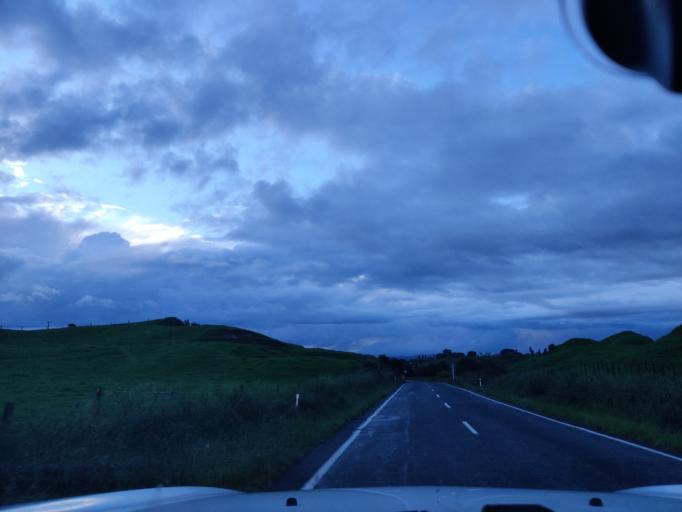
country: NZ
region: Waikato
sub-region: South Waikato District
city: Tokoroa
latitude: -38.2100
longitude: 175.8245
